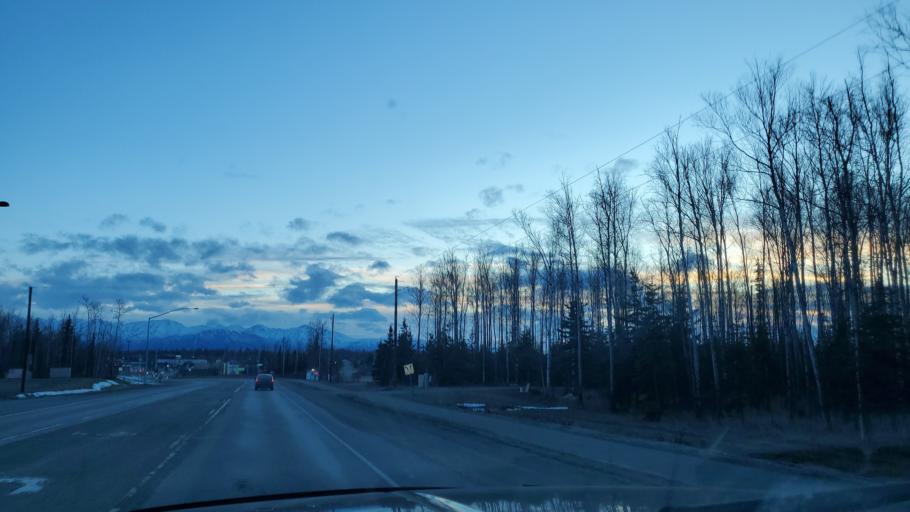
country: US
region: Alaska
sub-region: Matanuska-Susitna Borough
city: Wasilla
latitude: 61.5879
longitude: -149.4436
